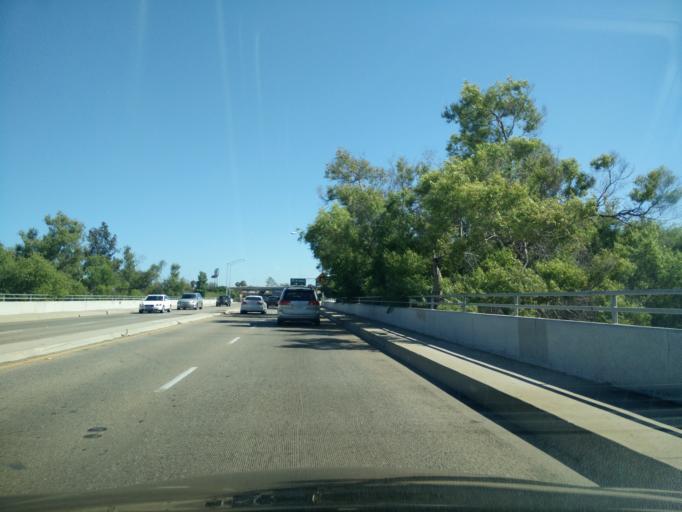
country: US
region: California
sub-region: San Diego County
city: San Diego
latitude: 32.7628
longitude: -117.1980
